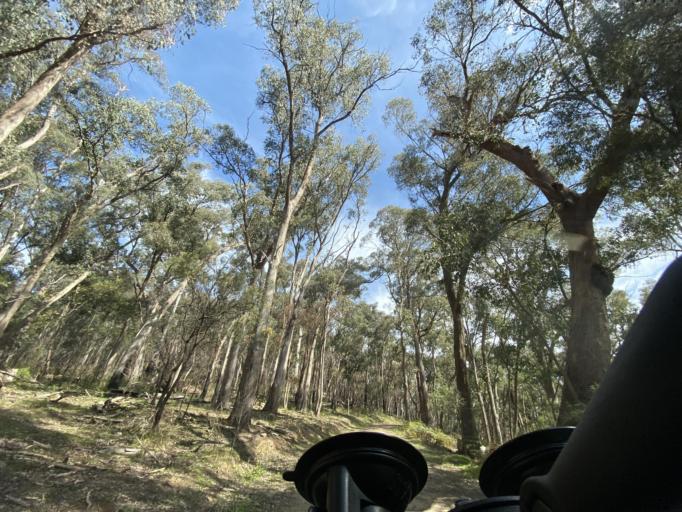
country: AU
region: Victoria
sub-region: Mansfield
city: Mansfield
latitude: -36.8335
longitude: 146.1009
